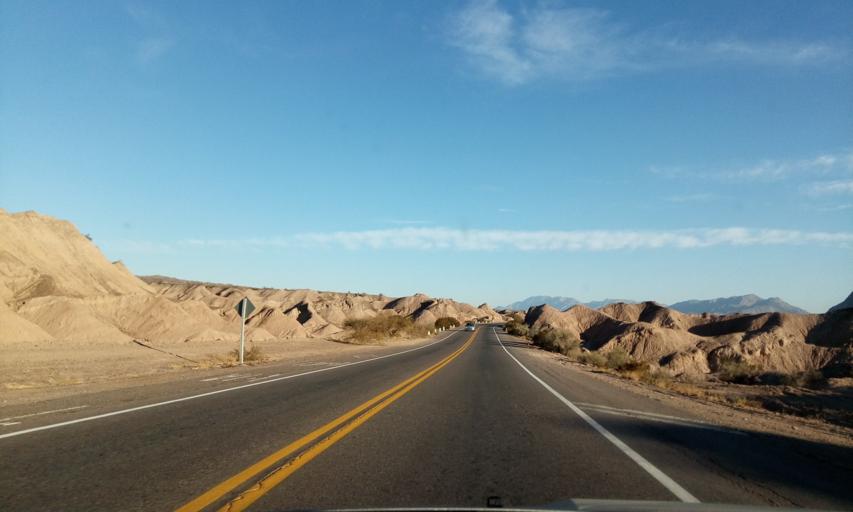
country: AR
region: San Juan
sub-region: Departamento de Rivadavia
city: Rivadavia
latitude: -31.4519
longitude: -68.6372
